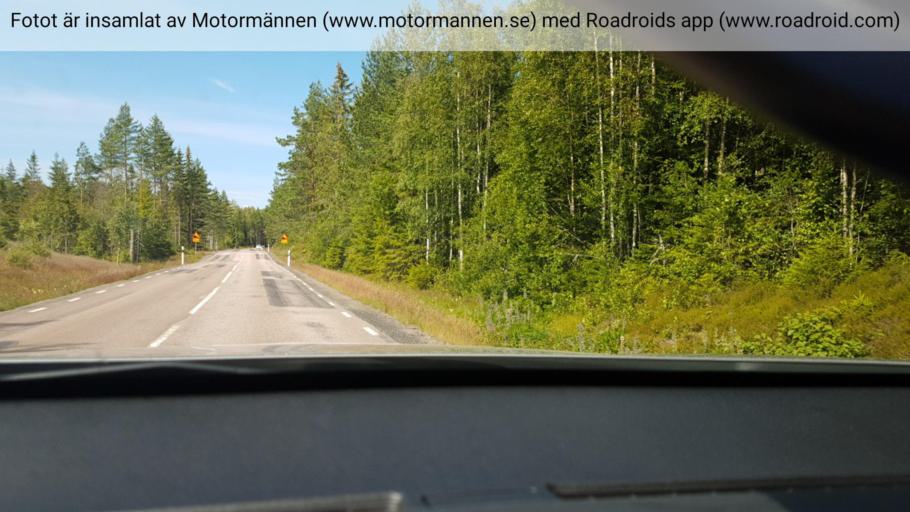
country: SE
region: Vaermland
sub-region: Sunne Kommun
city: Sunne
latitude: 59.8637
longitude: 13.2979
